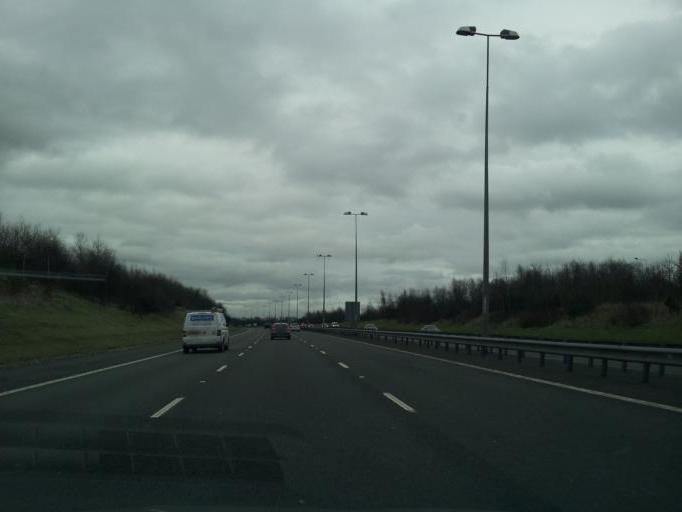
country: GB
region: England
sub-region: Staffordshire
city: Norton Canes
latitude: 52.6641
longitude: -1.9860
